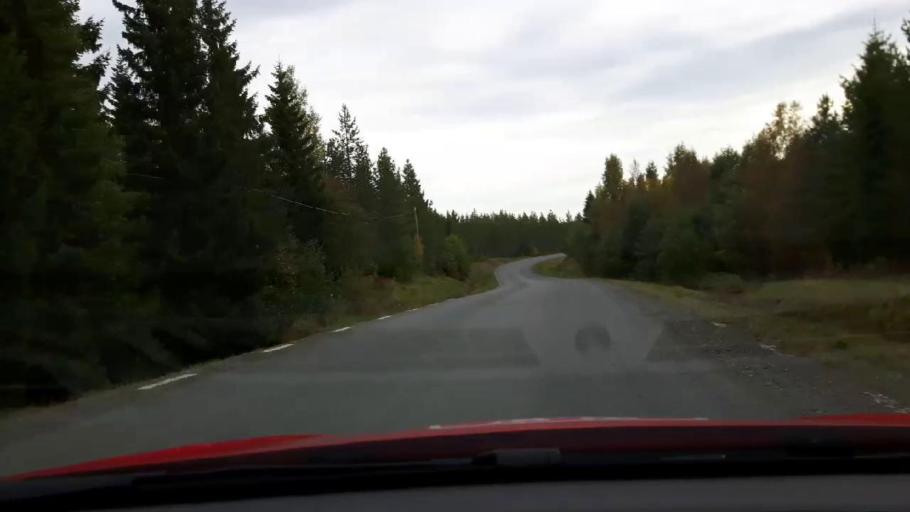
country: SE
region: Jaemtland
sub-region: Krokoms Kommun
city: Krokom
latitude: 63.2107
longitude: 14.1175
